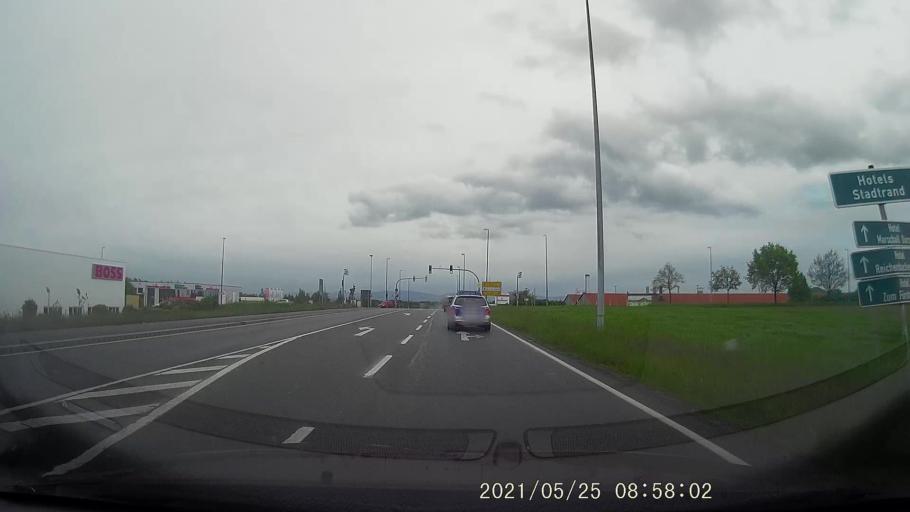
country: DE
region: Saxony
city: Goerlitz
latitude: 51.1884
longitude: 14.9563
